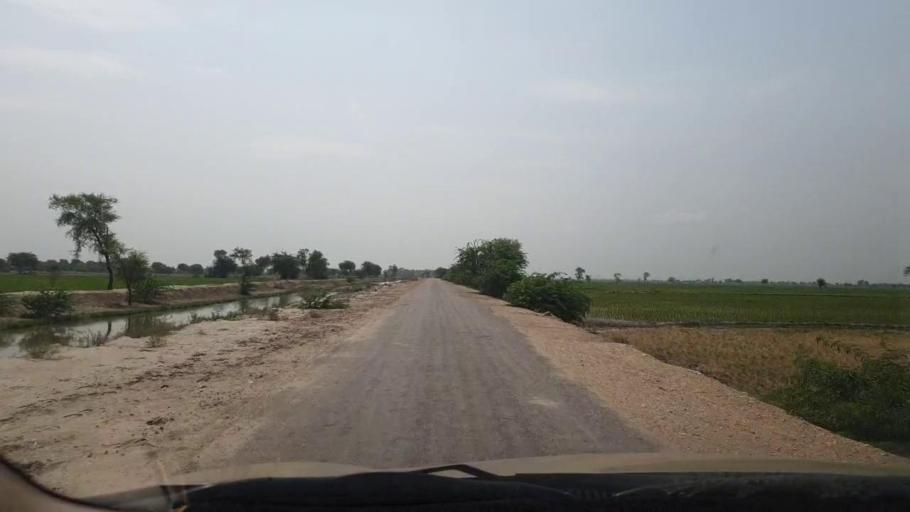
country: PK
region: Sindh
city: Goth Garelo
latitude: 27.5145
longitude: 68.1061
